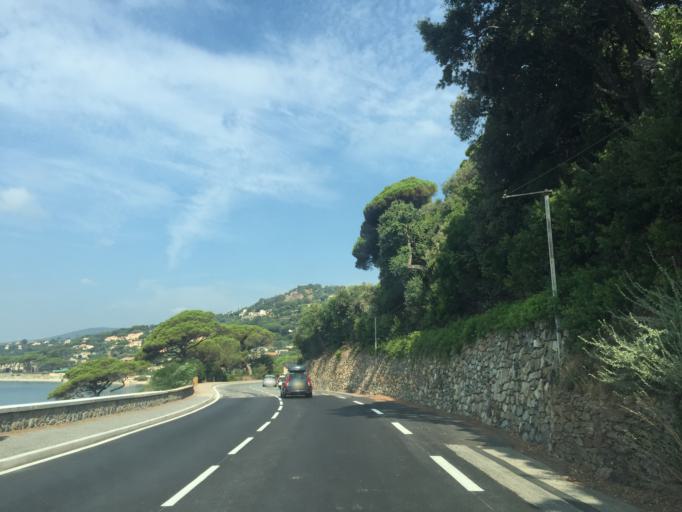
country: FR
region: Provence-Alpes-Cote d'Azur
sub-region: Departement du Var
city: Sainte-Maxime
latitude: 43.3137
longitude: 6.6642
